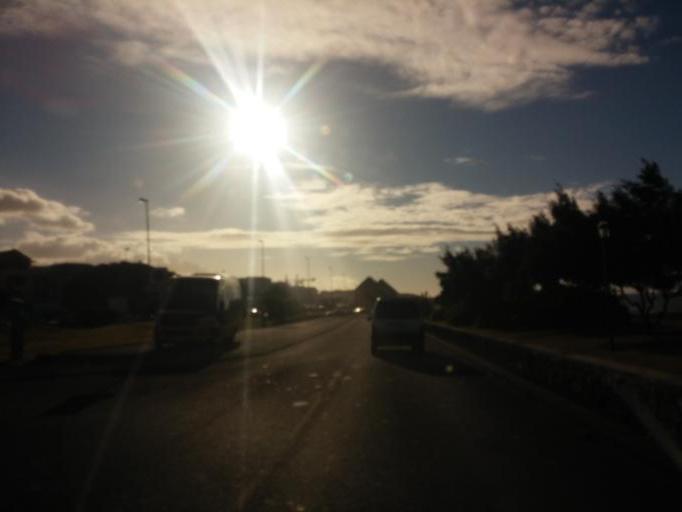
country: RE
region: Reunion
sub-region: Reunion
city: Saint-Denis
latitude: -20.8767
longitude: 55.4561
